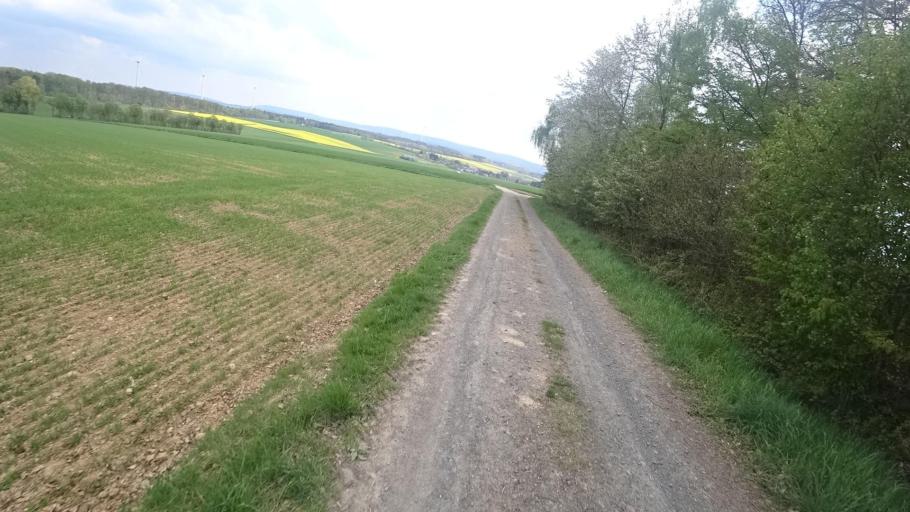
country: DE
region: Rheinland-Pfalz
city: Klosterkumbd
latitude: 50.0362
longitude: 7.5278
